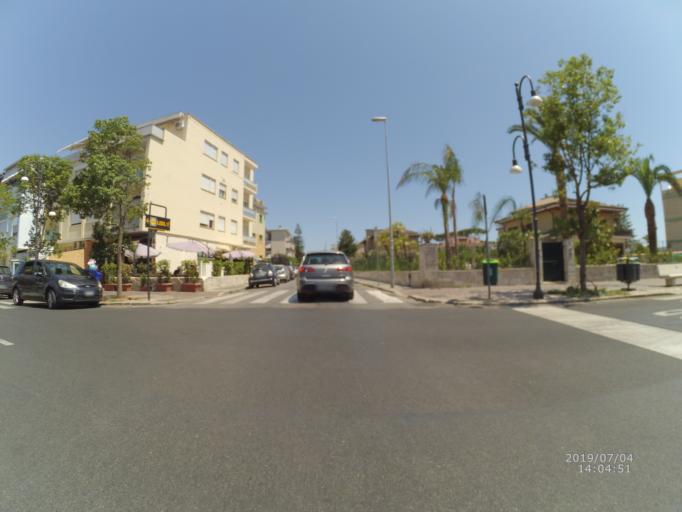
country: IT
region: Latium
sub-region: Provincia di Latina
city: Terracina
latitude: 41.2854
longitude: 13.2478
